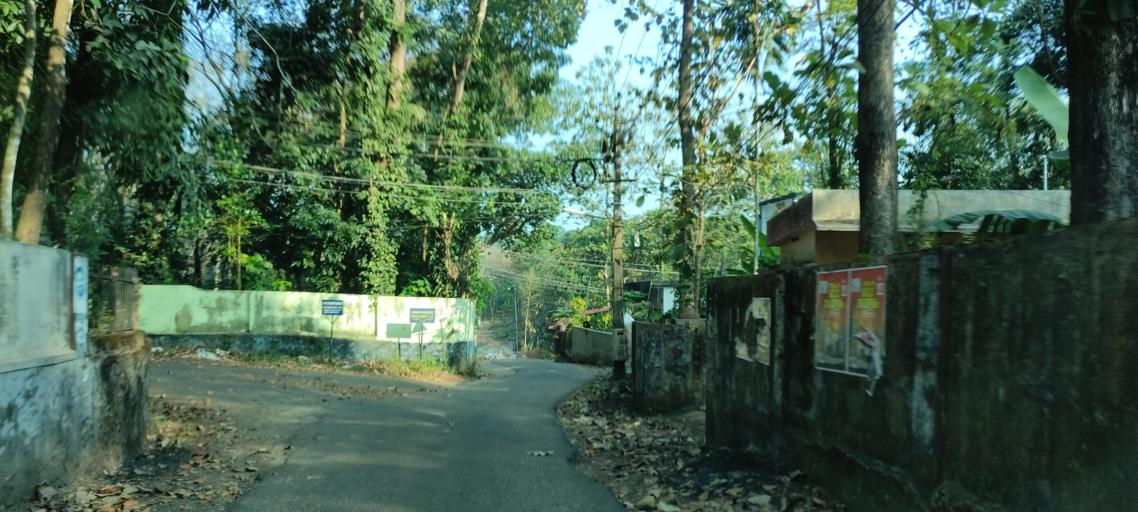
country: IN
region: Kerala
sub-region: Pattanamtitta
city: Adur
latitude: 9.1559
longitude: 76.7446
